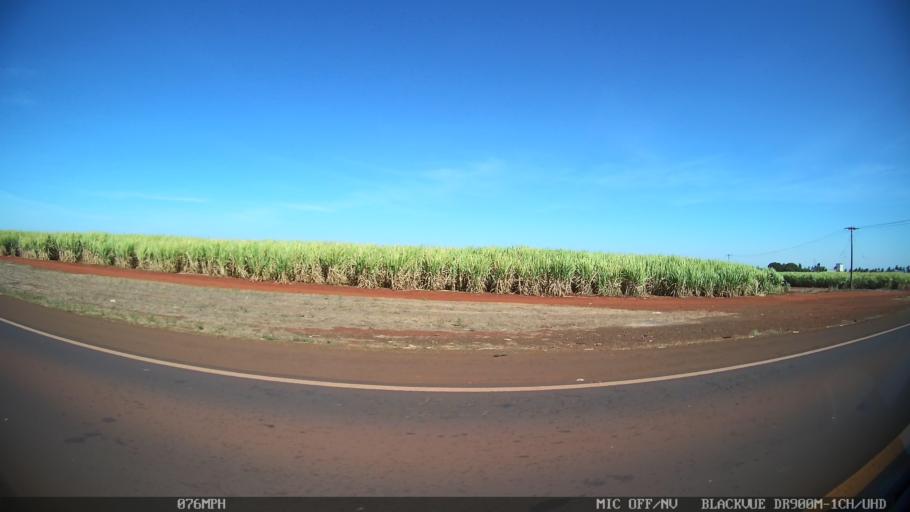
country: BR
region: Sao Paulo
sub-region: Guaira
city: Guaira
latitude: -20.4443
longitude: -48.2853
